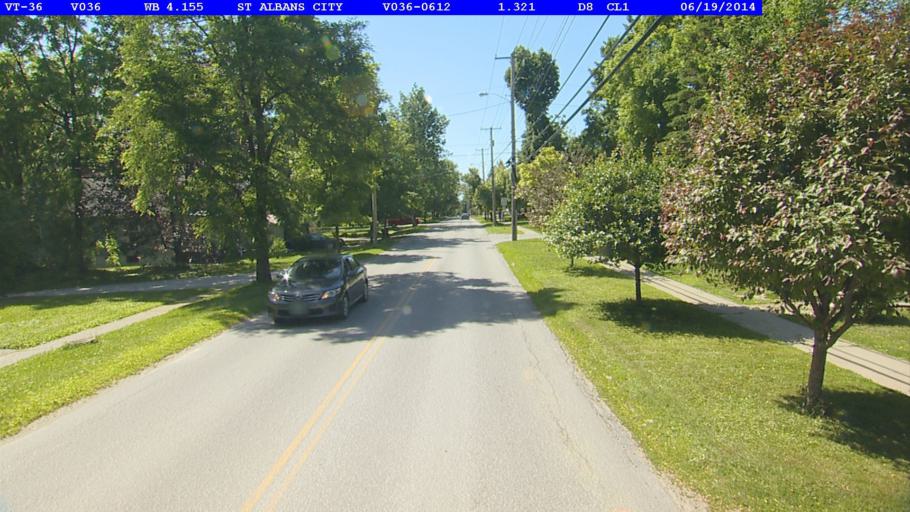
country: US
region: Vermont
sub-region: Franklin County
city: Saint Albans
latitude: 44.8075
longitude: -73.0751
